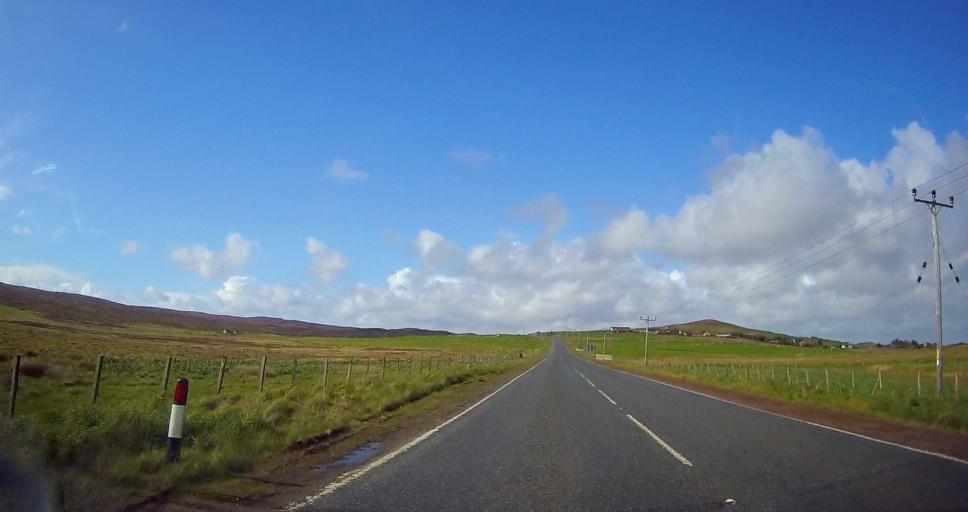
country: GB
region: Scotland
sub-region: Shetland Islands
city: Lerwick
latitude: 60.1924
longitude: -1.2320
